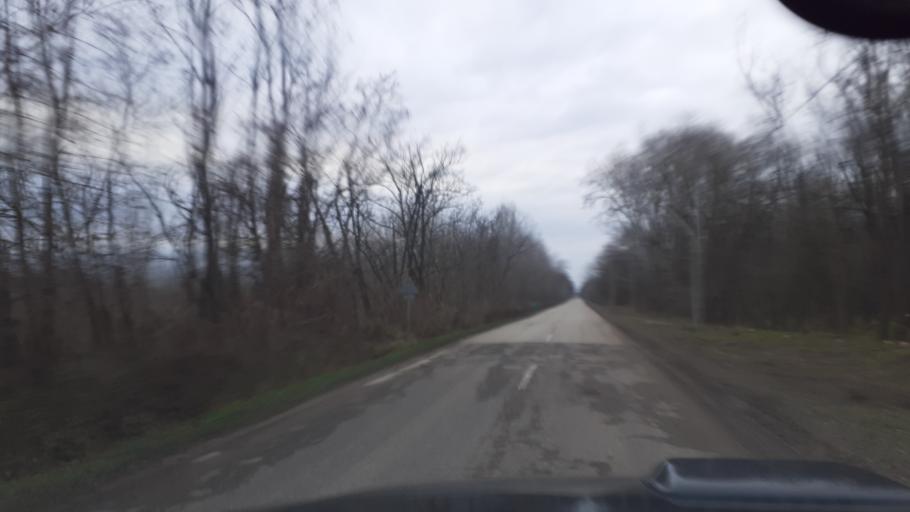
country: HU
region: Bacs-Kiskun
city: Szalkszentmarton
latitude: 46.9487
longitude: 19.0652
